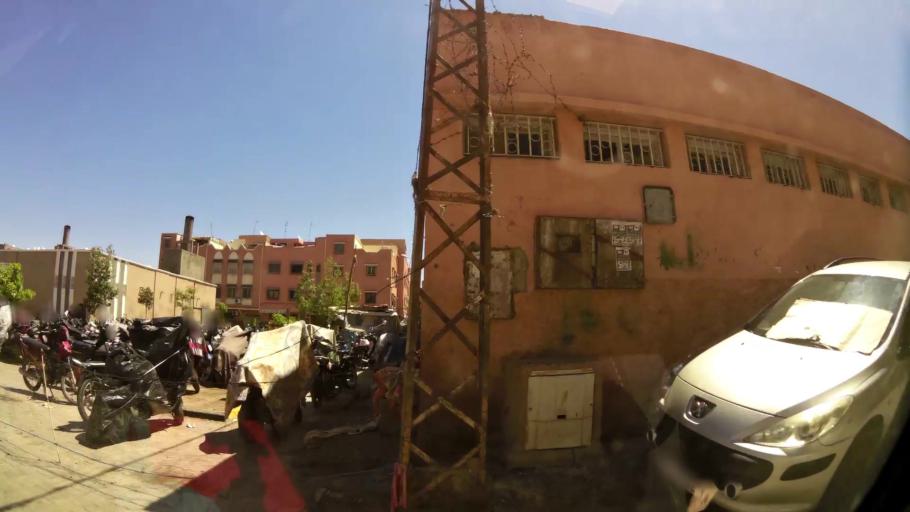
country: MA
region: Marrakech-Tensift-Al Haouz
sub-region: Marrakech
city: Marrakesh
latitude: 31.6548
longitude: -7.9917
